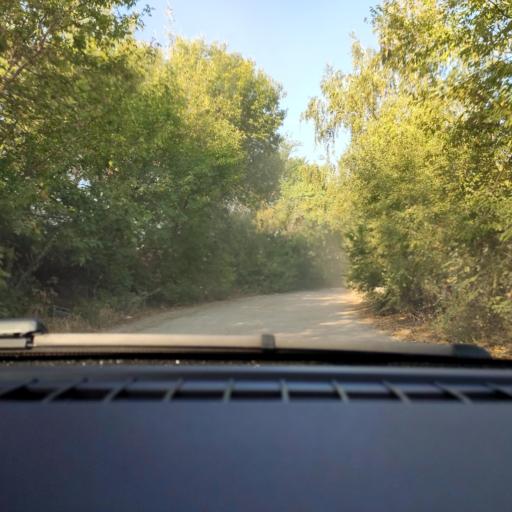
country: RU
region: Voronezj
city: Voronezh
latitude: 51.6453
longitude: 39.2786
